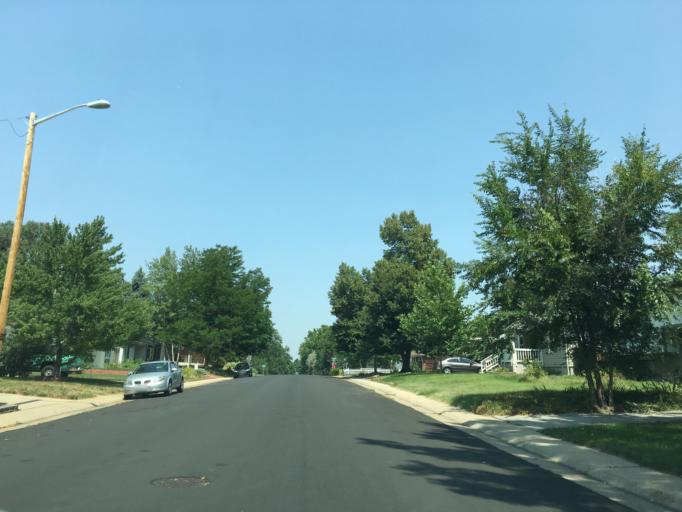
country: US
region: Colorado
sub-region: Arapahoe County
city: Glendale
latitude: 39.7099
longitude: -104.9200
